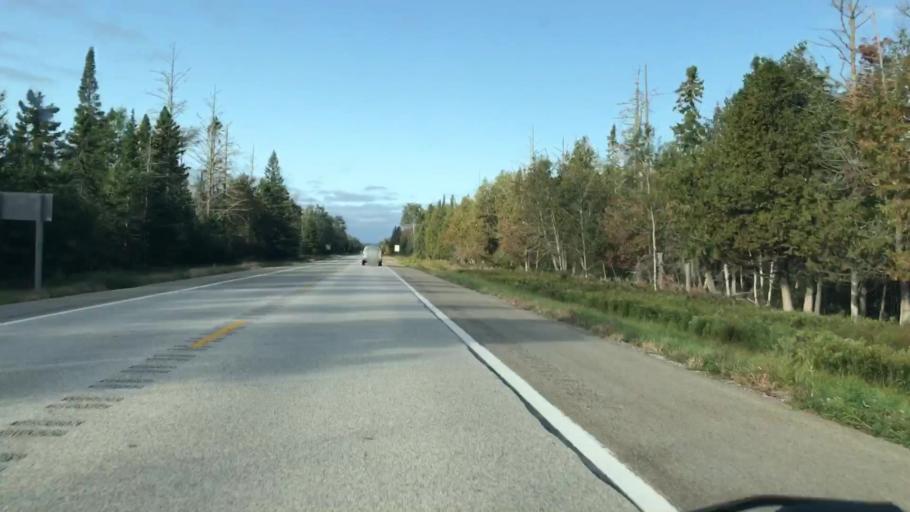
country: US
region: Michigan
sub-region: Luce County
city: Newberry
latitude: 46.3277
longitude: -85.1615
